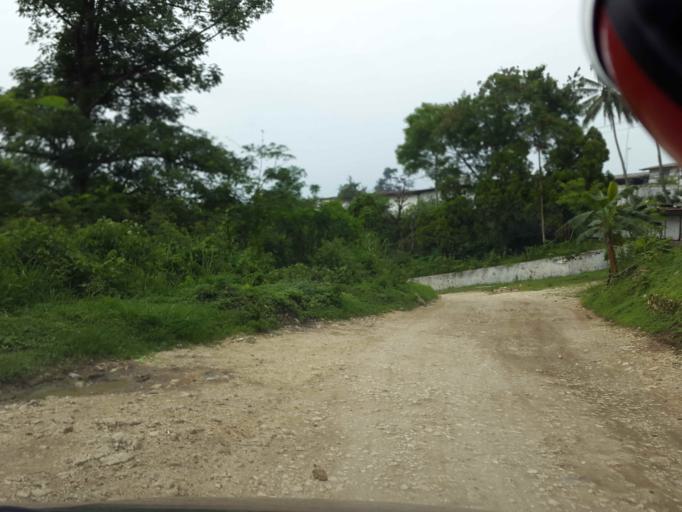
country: ID
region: West Java
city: Padalarang
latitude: -6.8424
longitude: 107.4209
